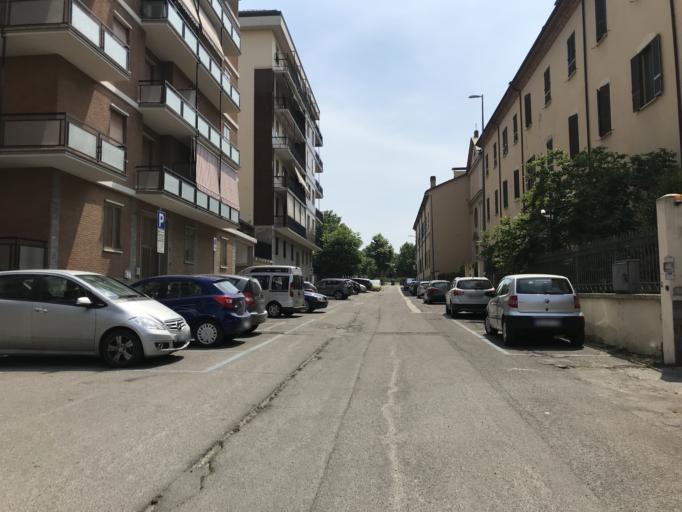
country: IT
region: Emilia-Romagna
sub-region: Provincia di Piacenza
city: Piacenza
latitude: 45.0455
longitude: 9.7003
